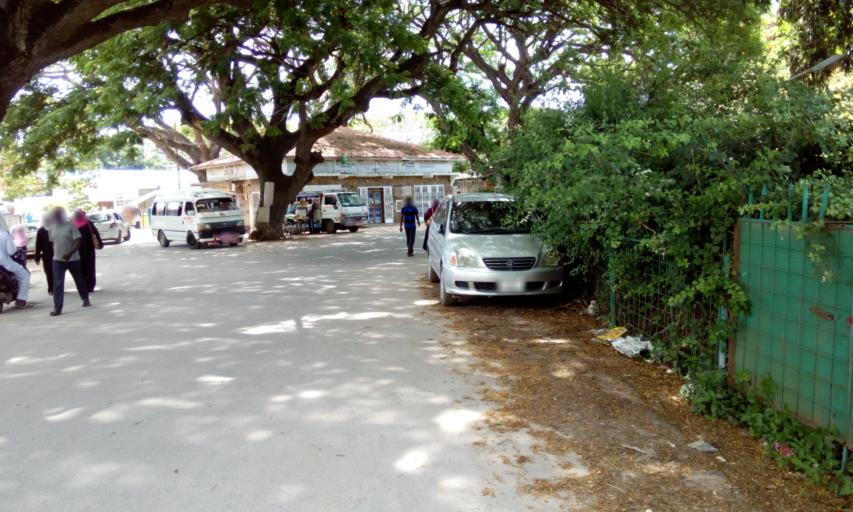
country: TZ
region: Zanzibar Urban/West
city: Zanzibar
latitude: -6.1656
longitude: 39.1940
